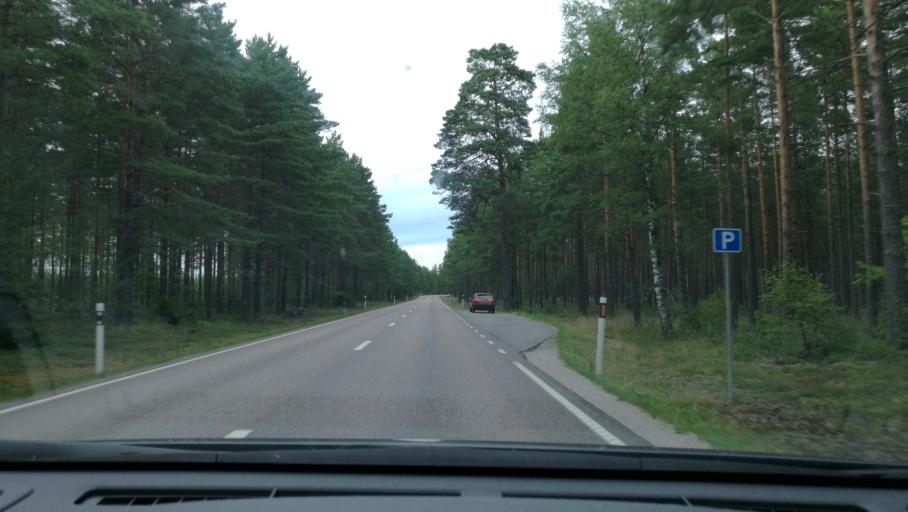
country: SE
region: Vaestmanland
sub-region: Kungsors Kommun
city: Kungsoer
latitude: 59.3436
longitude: 16.1122
